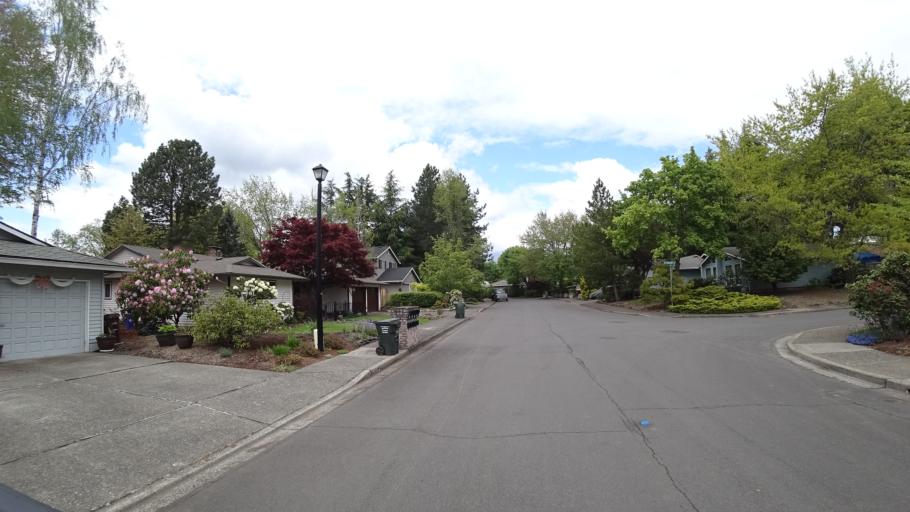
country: US
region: Oregon
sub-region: Washington County
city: Rockcreek
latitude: 45.5602
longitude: -122.8927
